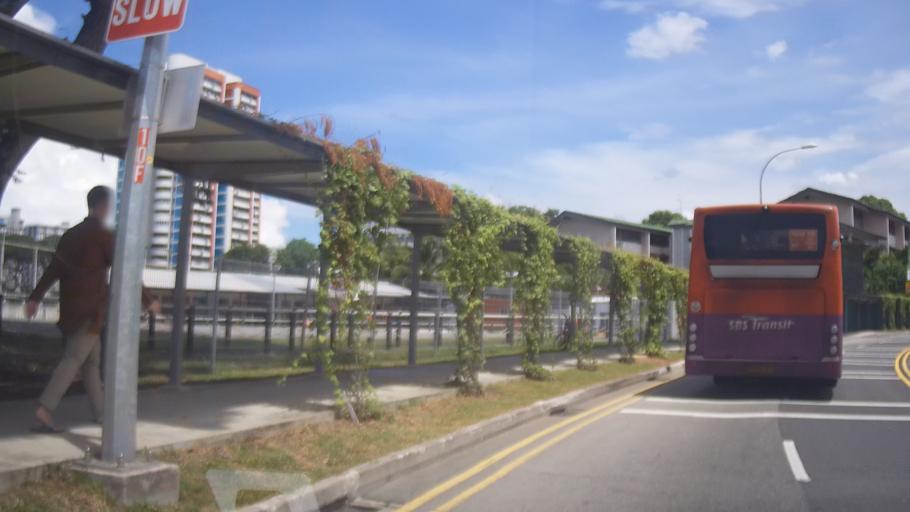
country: SG
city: Singapore
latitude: 1.3251
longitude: 103.8833
